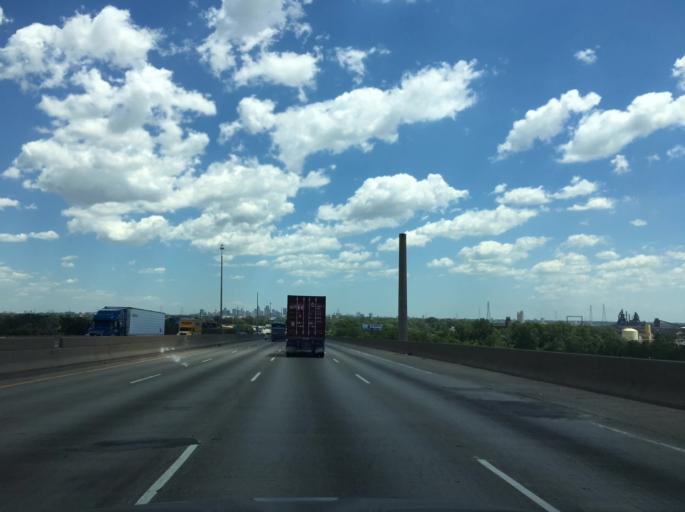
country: US
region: Michigan
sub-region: Wayne County
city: River Rouge
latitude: 42.2879
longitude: -83.1370
